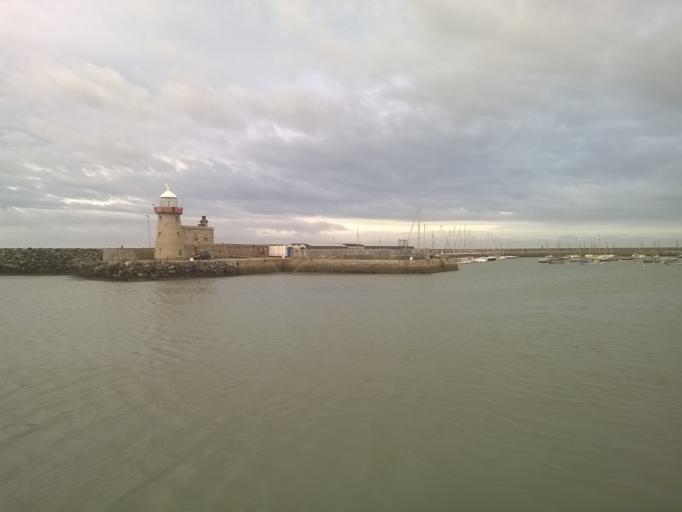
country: IE
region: Leinster
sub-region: Fingal County
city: Howth
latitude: 53.3930
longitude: -6.0684
